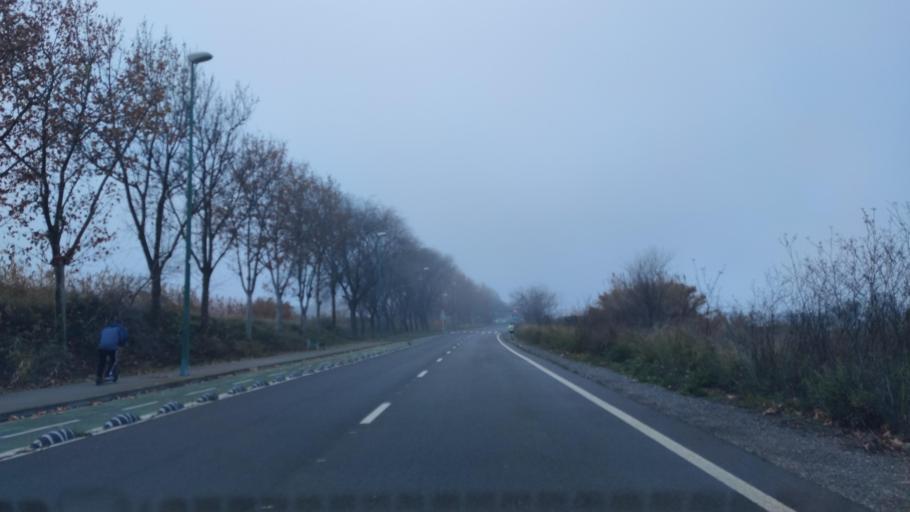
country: ES
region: Aragon
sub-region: Provincia de Zaragoza
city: Utebo
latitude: 41.7138
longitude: -1.0113
